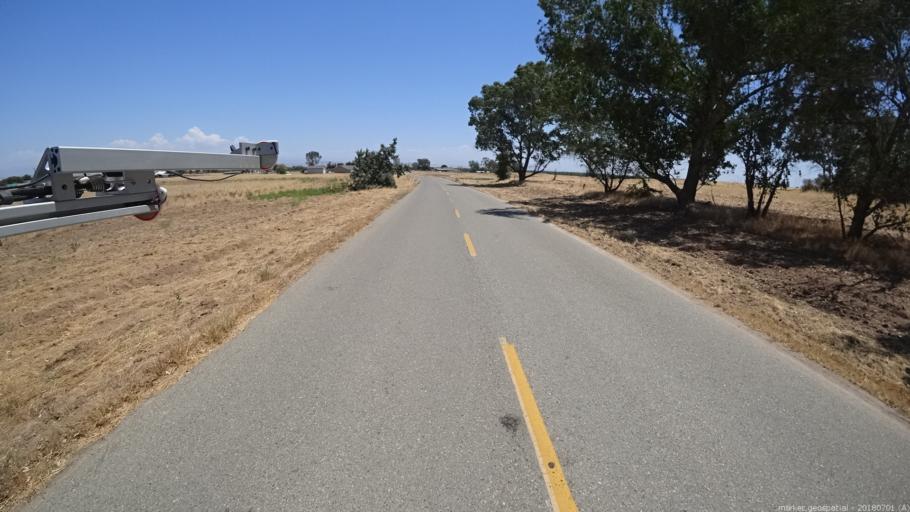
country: US
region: California
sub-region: Madera County
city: Madera Acres
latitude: 37.0520
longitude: -119.9886
